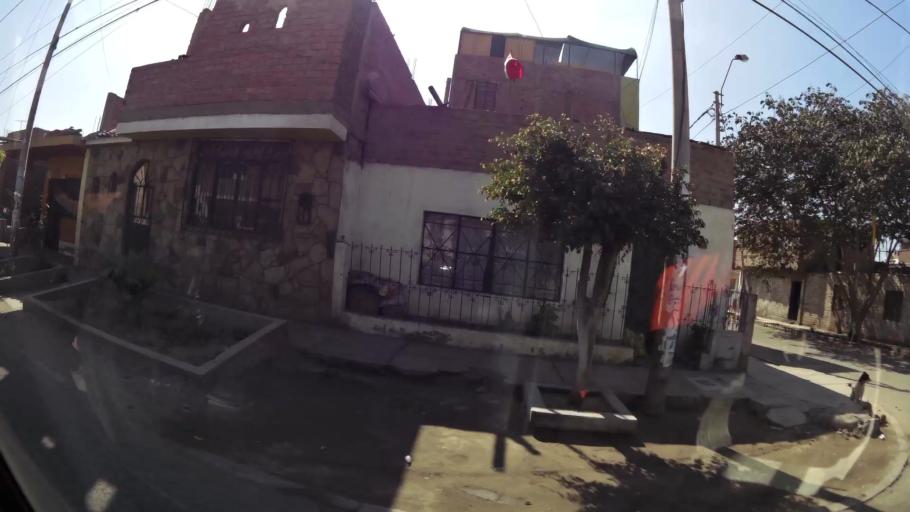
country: PE
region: Ica
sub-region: Provincia de Ica
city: Ica
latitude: -14.0686
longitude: -75.7211
